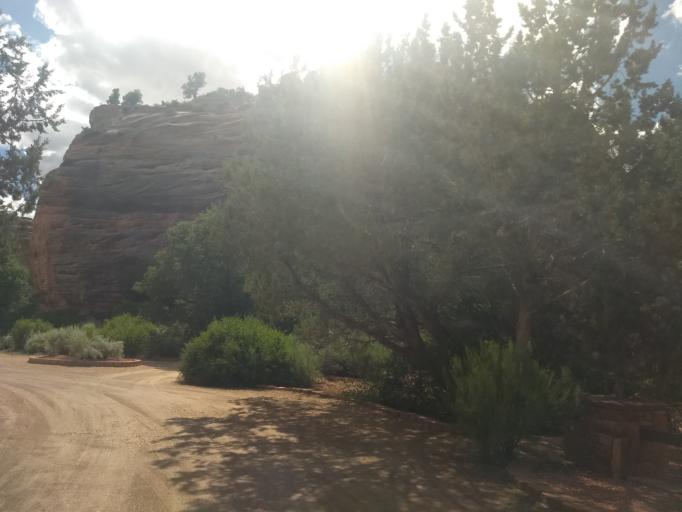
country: US
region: Utah
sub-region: Kane County
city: Kanab
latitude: 37.1475
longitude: -112.5400
